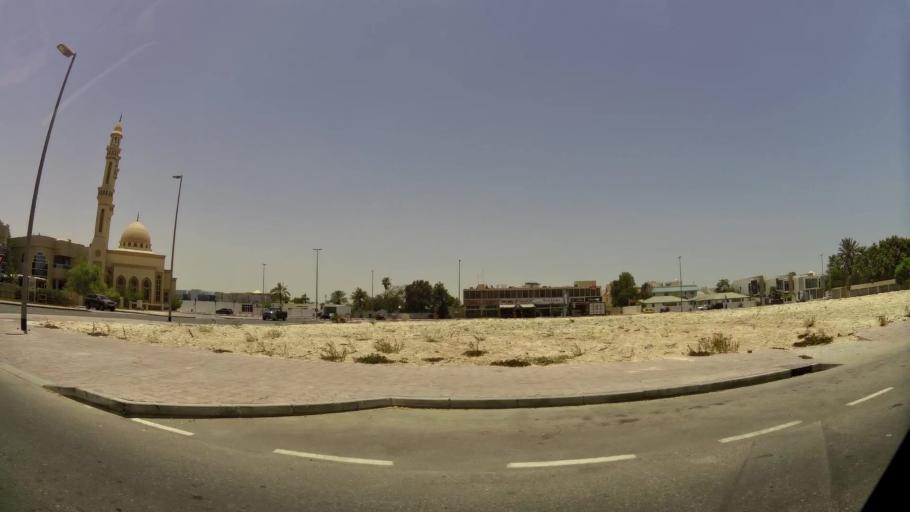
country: AE
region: Dubai
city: Dubai
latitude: 25.1739
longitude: 55.2228
